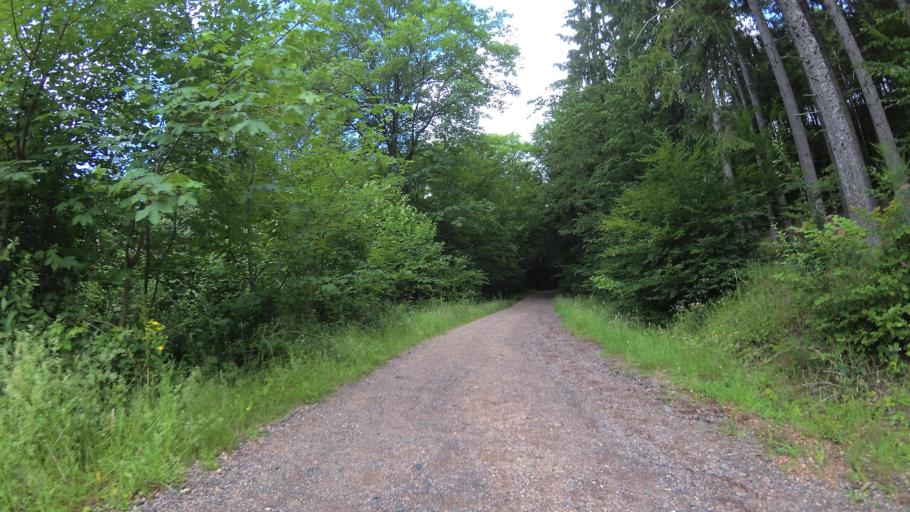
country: DE
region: Saarland
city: Nonnweiler
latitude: 49.6155
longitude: 6.9738
